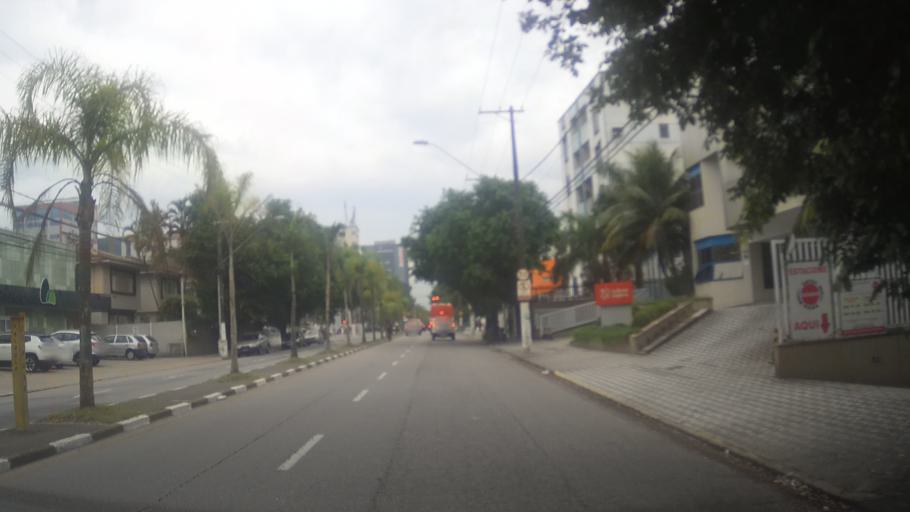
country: BR
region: Sao Paulo
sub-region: Santos
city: Santos
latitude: -23.9592
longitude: -46.3230
